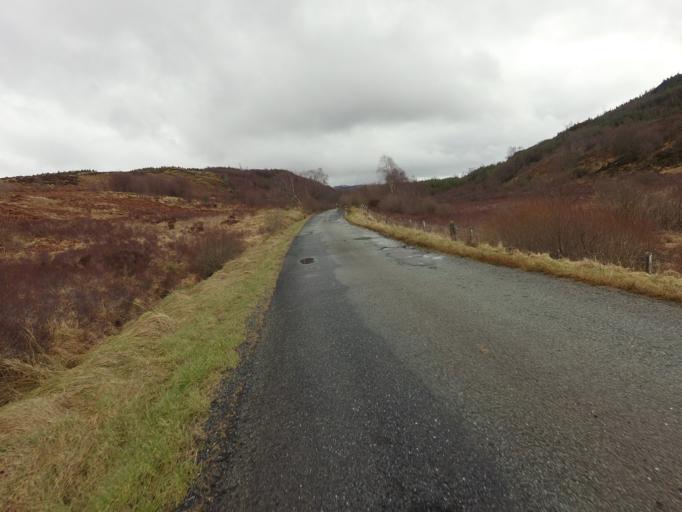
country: GB
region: Scotland
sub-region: West Dunbartonshire
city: Balloch
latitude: 56.2450
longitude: -4.5765
